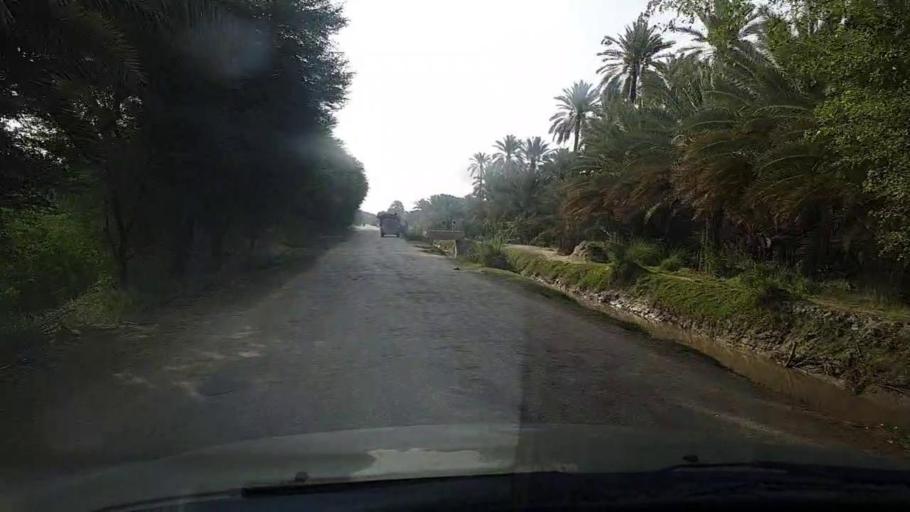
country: PK
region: Sindh
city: Pir jo Goth
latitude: 27.5622
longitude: 68.5416
